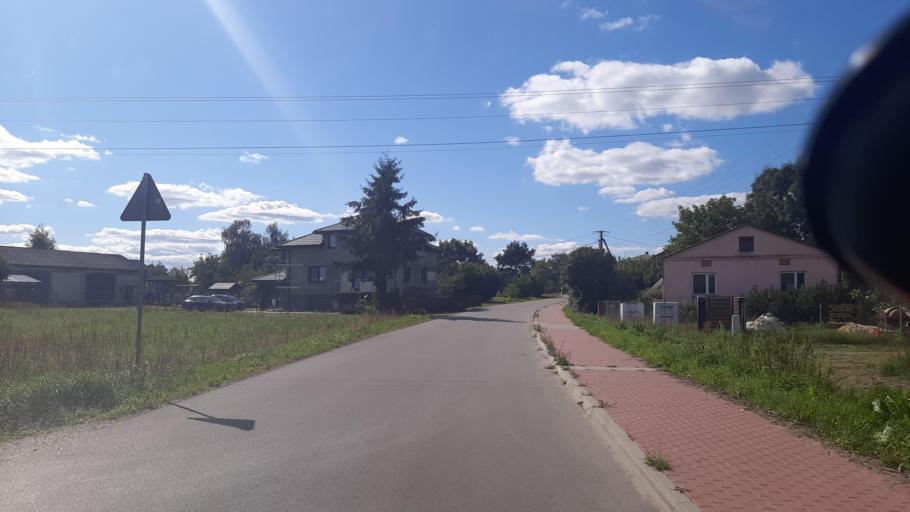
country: PL
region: Lublin Voivodeship
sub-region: Powiat lubelski
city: Garbow
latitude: 51.4023
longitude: 22.3361
